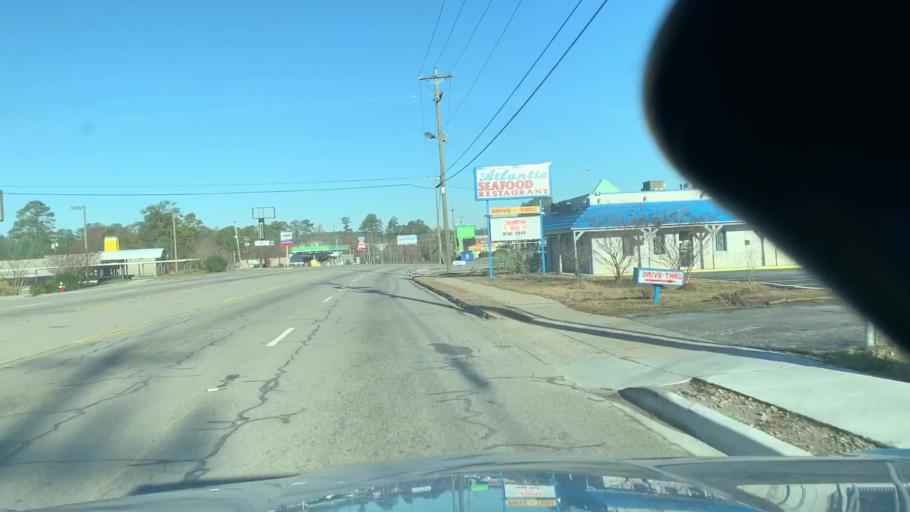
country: US
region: South Carolina
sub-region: Richland County
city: Dentsville
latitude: 34.0568
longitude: -80.9493
